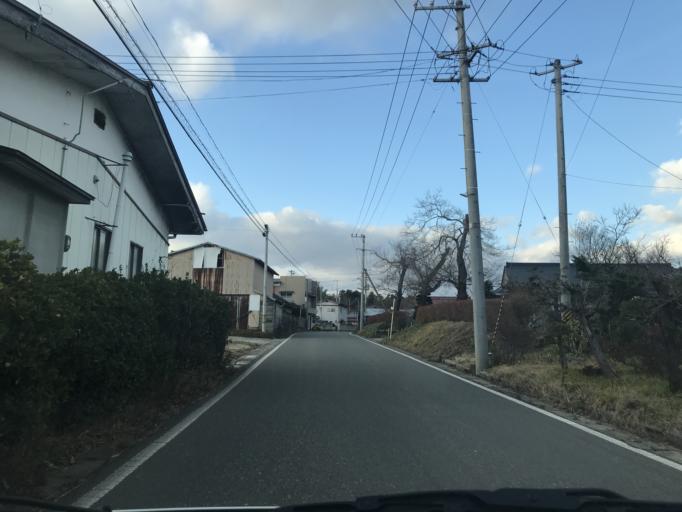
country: JP
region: Miyagi
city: Kogota
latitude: 38.6395
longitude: 141.0522
